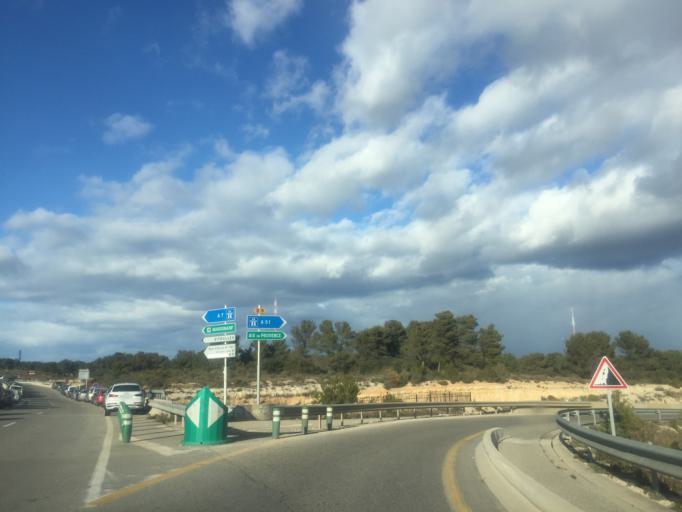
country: FR
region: Provence-Alpes-Cote d'Azur
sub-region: Departement des Bouches-du-Rhone
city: Les Pennes-Mirabeau
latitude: 43.4545
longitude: 5.3189
